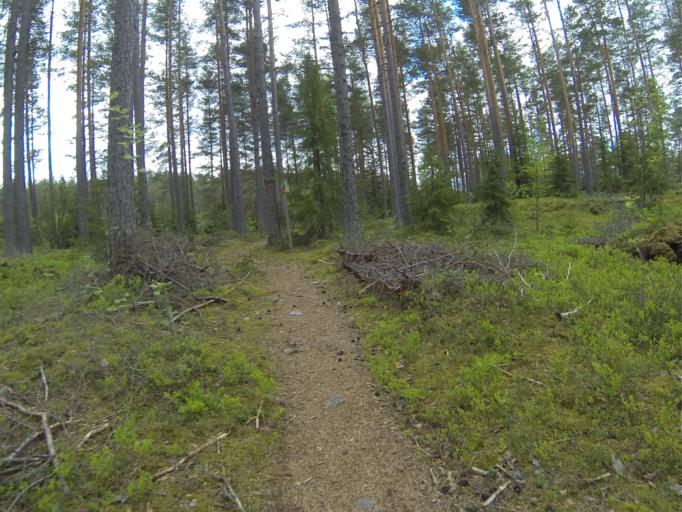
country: FI
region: Varsinais-Suomi
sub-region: Salo
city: Salo
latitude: 60.3533
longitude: 23.1112
